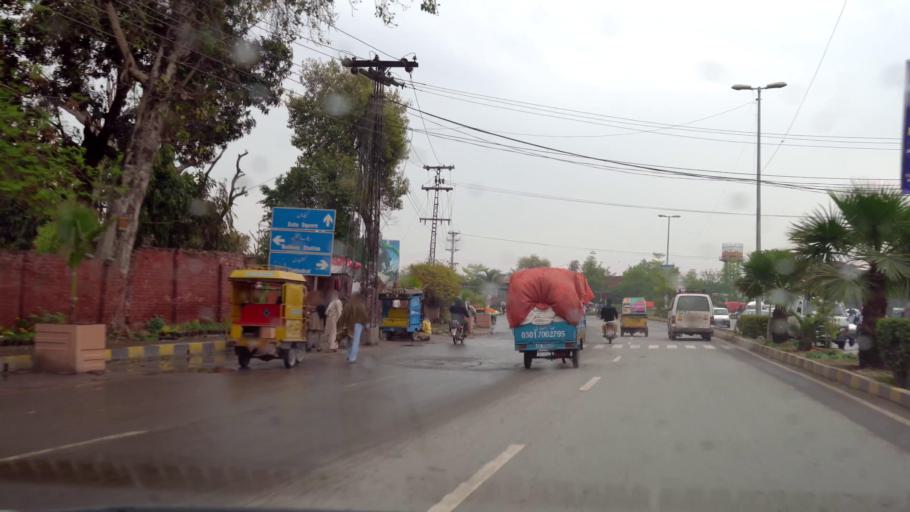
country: PK
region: Punjab
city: Faisalabad
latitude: 31.4175
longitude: 73.0904
